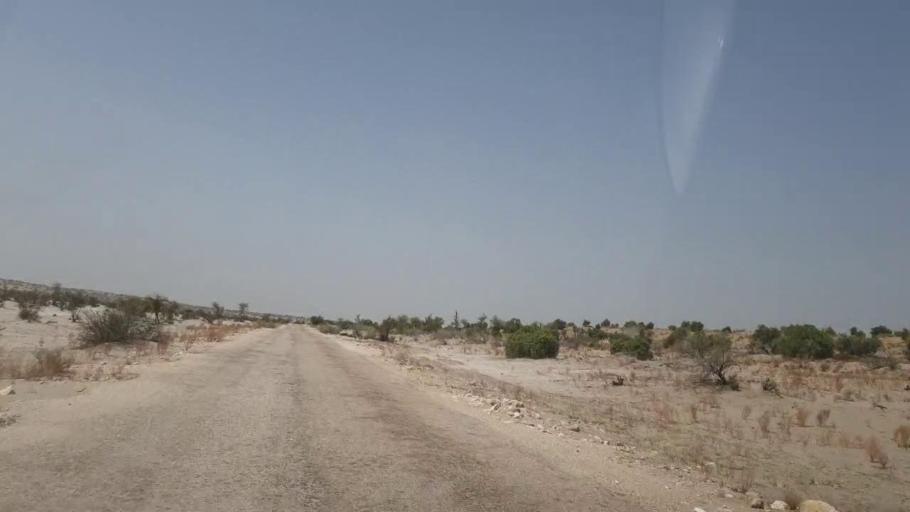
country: PK
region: Sindh
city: Khanpur
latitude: 27.3448
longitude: 69.3183
